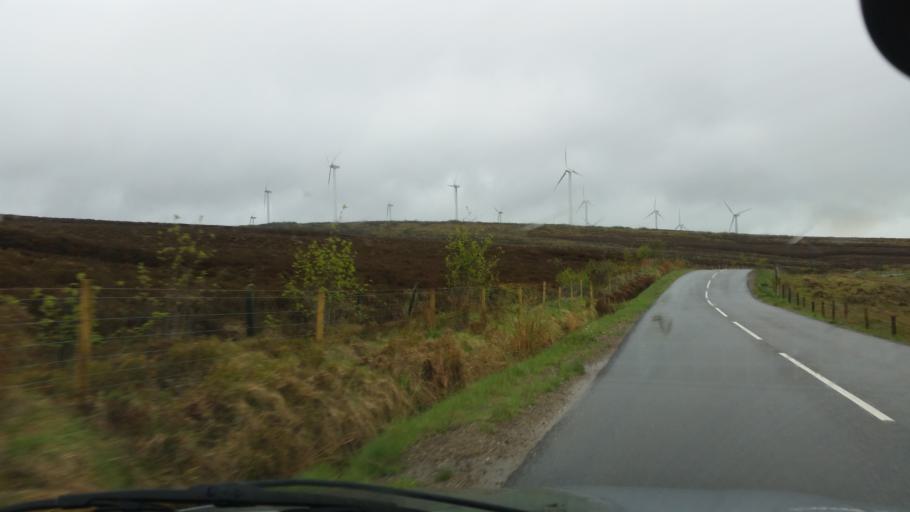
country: GB
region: Northern Ireland
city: Fivemiletown
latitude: 54.4386
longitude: -7.3270
